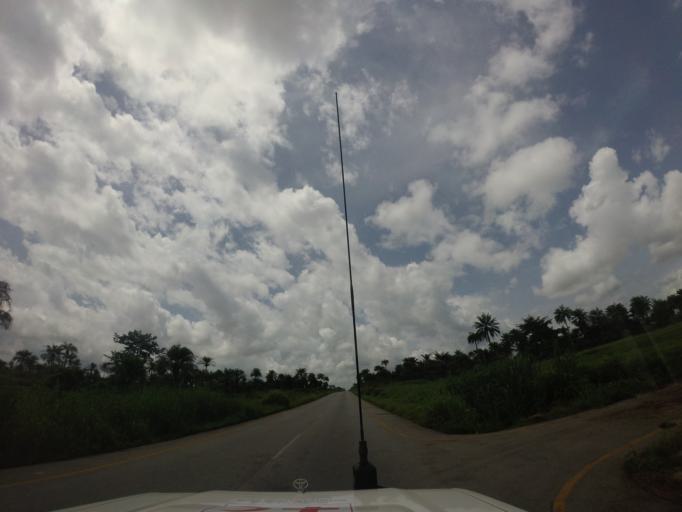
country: SL
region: Northern Province
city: Rokupr
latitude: 8.4699
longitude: -12.4752
